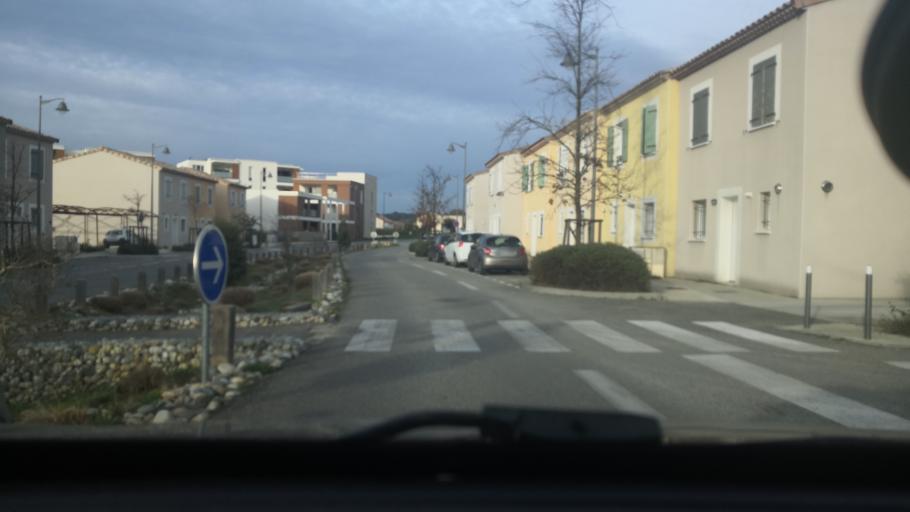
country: FR
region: Rhone-Alpes
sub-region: Departement de la Drome
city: Montelimar
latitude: 44.5384
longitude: 4.7692
